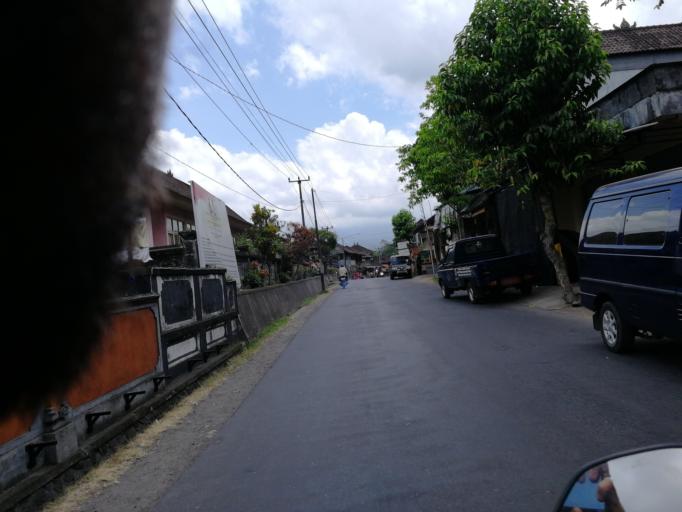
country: ID
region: Bali
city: Banjar Wangsian
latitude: -8.4641
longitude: 115.4479
